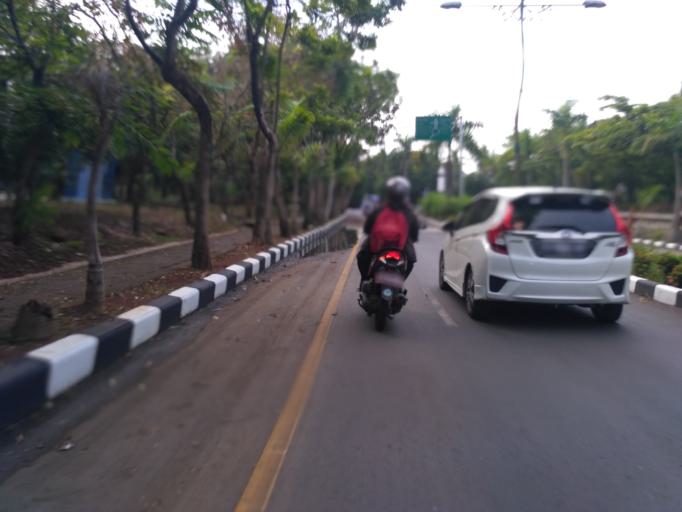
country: ID
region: Central Java
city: Semarang
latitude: -7.0526
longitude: 110.4398
